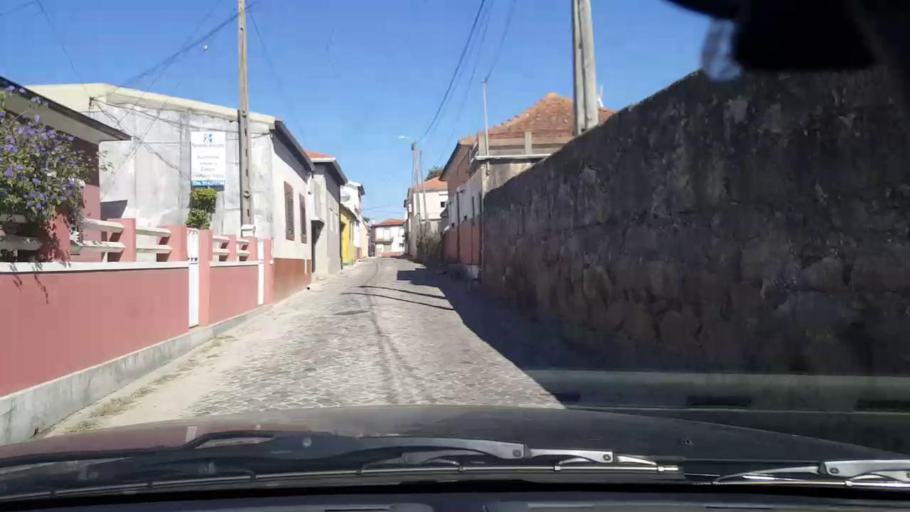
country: PT
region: Porto
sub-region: Maia
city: Gemunde
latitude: 41.2869
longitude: -8.6740
